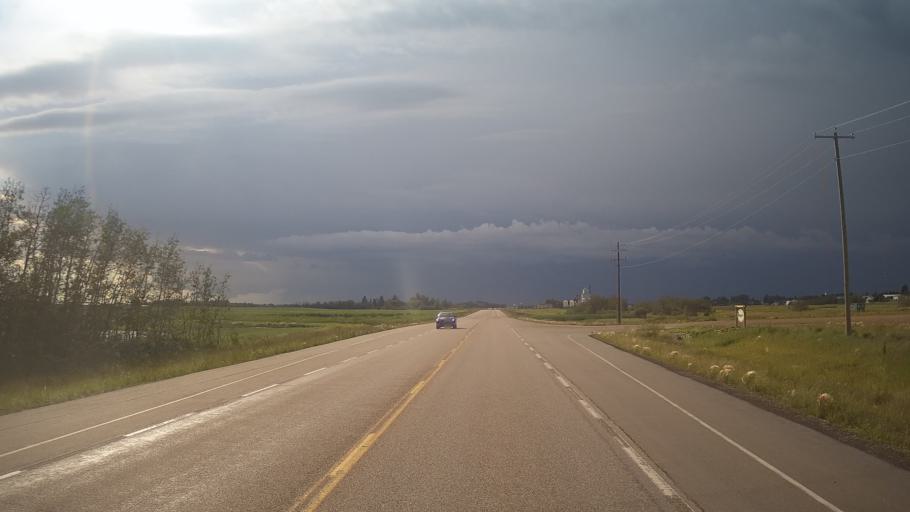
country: CA
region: Alberta
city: Vegreville
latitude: 53.2246
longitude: -112.2271
